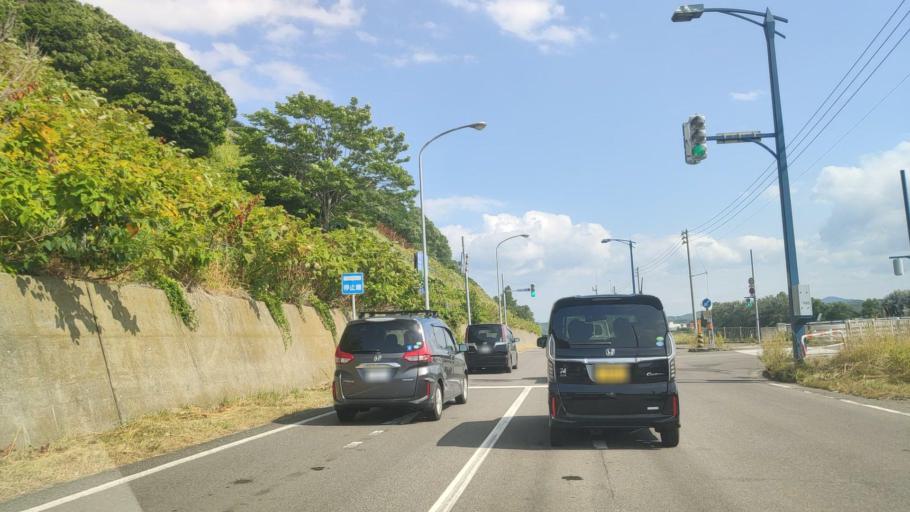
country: JP
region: Hokkaido
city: Rumoi
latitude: 43.9478
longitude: 141.6505
